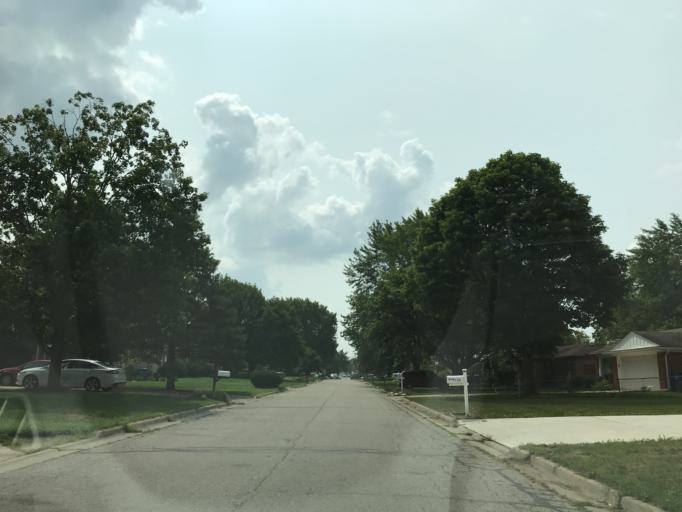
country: US
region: Michigan
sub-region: Washtenaw County
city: Ypsilanti
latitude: 42.2482
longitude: -83.6702
